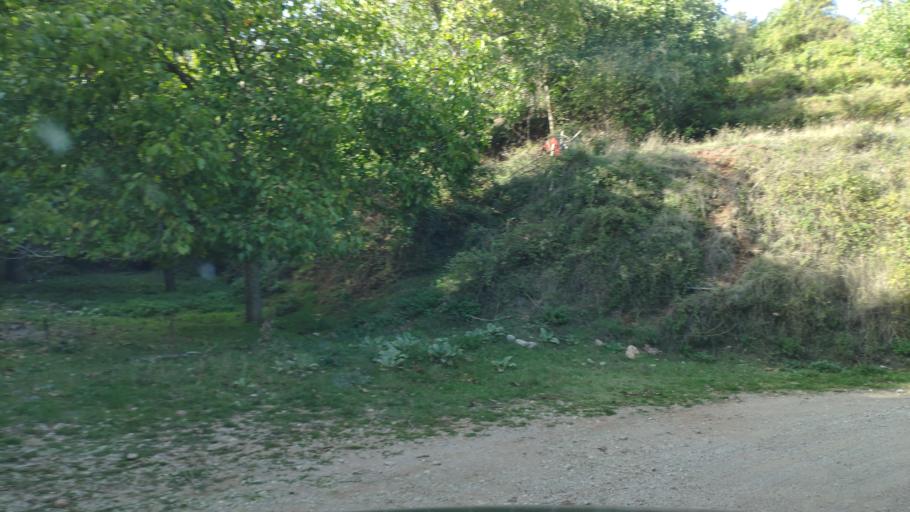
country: GR
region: West Greece
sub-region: Nomos Achaias
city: Aiyira
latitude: 37.9911
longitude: 22.3489
